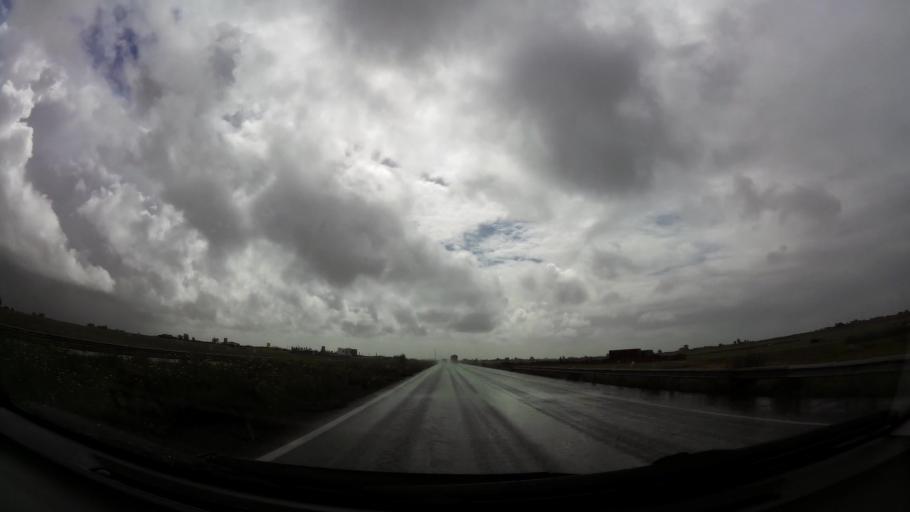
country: MA
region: Grand Casablanca
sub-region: Nouaceur
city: Dar Bouazza
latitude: 33.3918
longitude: -7.8660
